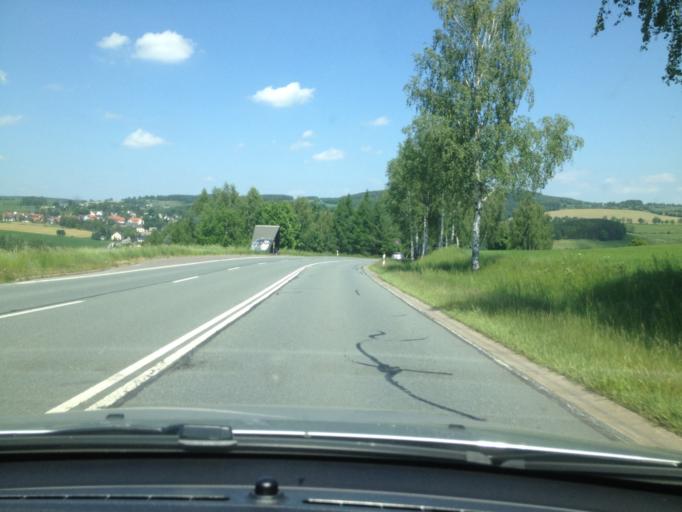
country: DE
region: Saxony
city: Wiesa
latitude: 50.6028
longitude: 12.9983
